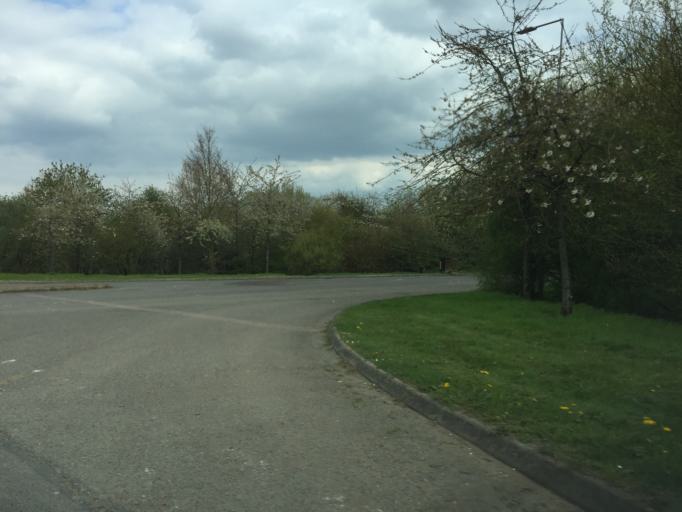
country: GB
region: England
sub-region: Milton Keynes
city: Milton Keynes
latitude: 52.0208
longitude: -0.7654
